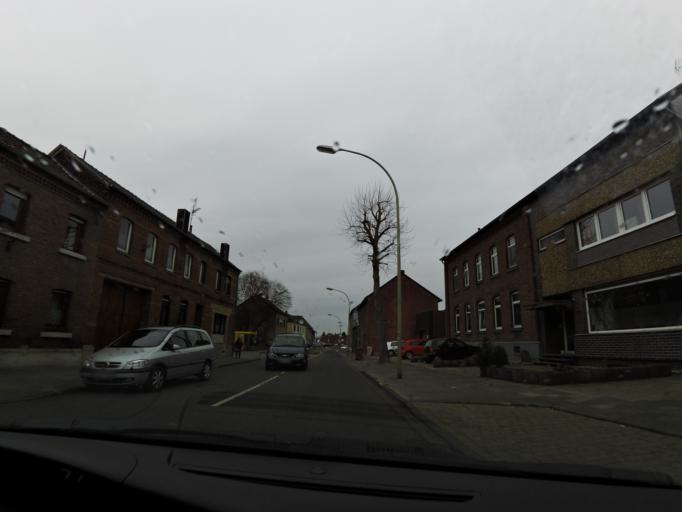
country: DE
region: North Rhine-Westphalia
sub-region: Regierungsbezirk Koln
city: Ubach-Palenberg
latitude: 50.9302
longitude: 6.0714
